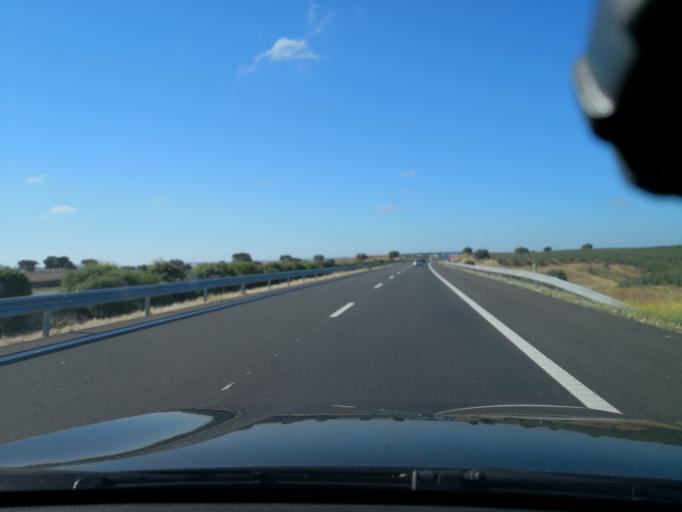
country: PT
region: Beja
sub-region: Aljustrel
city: Aljustrel
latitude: 37.9349
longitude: -8.2434
